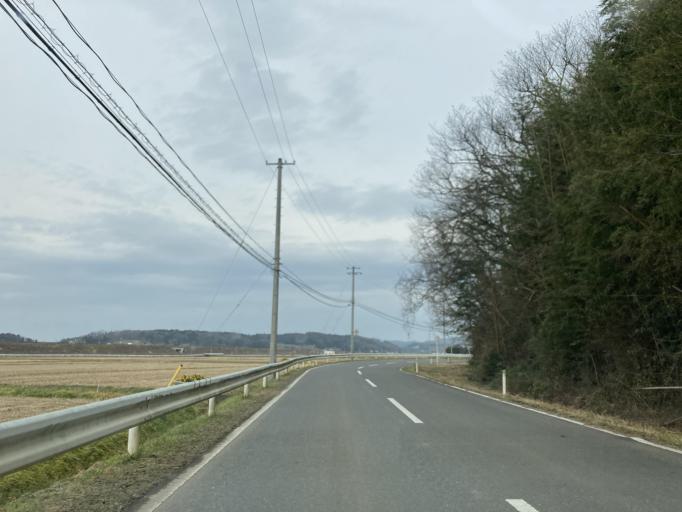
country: JP
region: Miyagi
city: Wakuya
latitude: 38.6859
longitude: 141.2750
